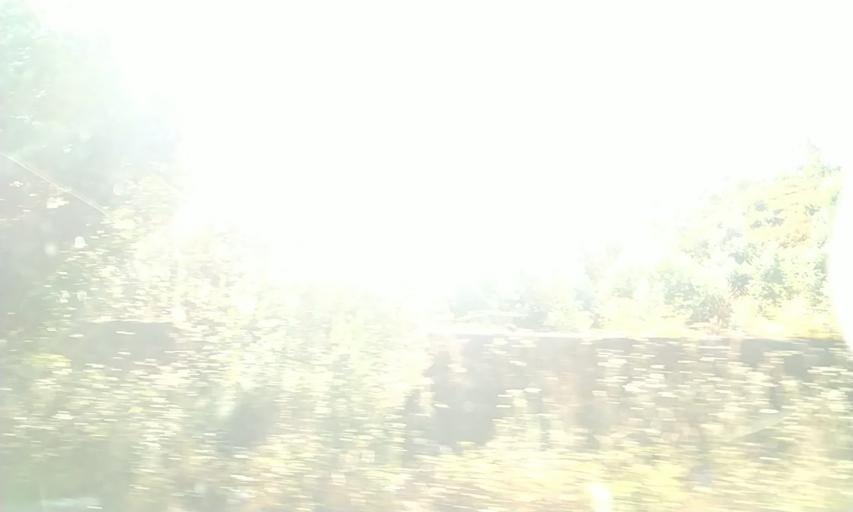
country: PT
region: Porto
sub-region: Pacos de Ferreira
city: Seroa
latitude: 41.2699
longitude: -8.4703
